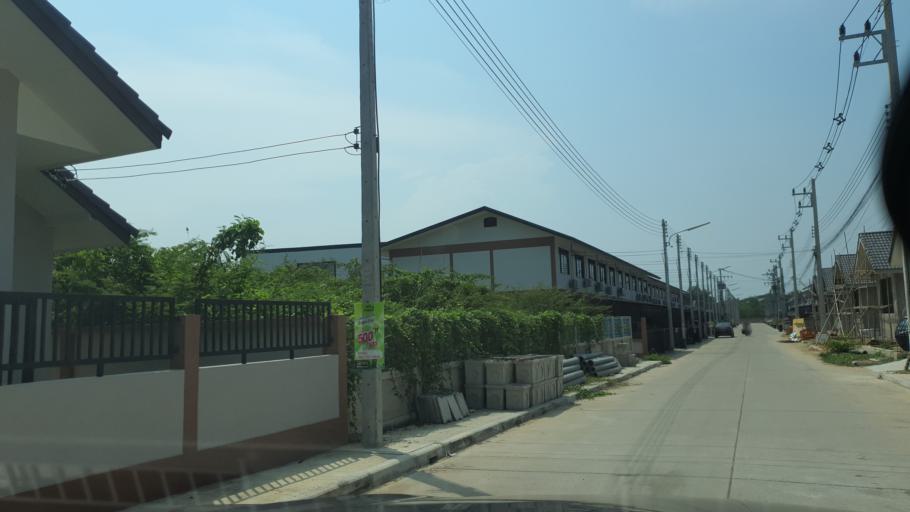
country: TH
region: Chiang Mai
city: San Kamphaeng
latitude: 18.7407
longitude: 99.1087
